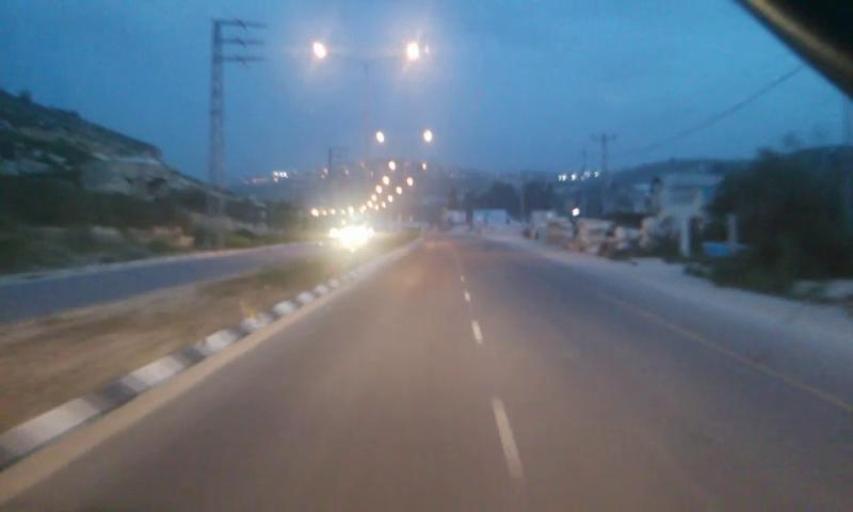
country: PS
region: West Bank
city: Dayr Sharaf
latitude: 32.2457
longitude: 35.1938
